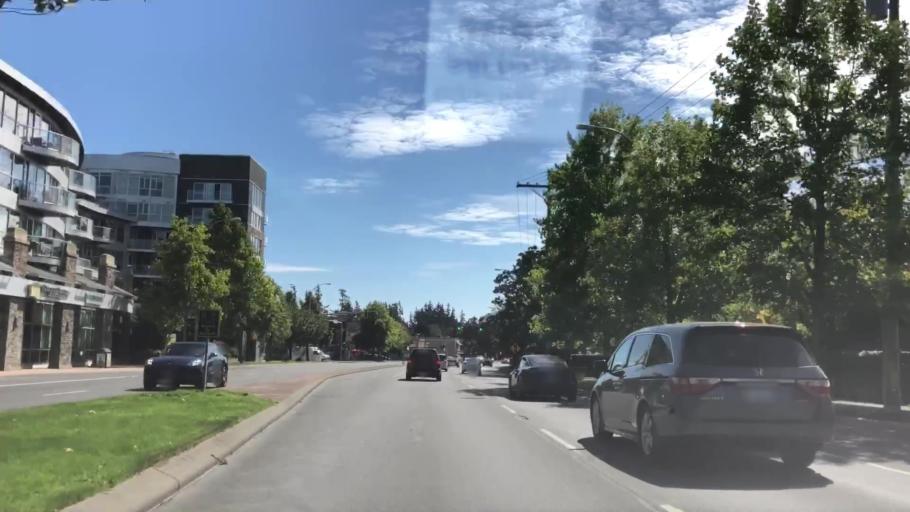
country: CA
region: British Columbia
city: Langford
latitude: 48.4505
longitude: -123.4953
